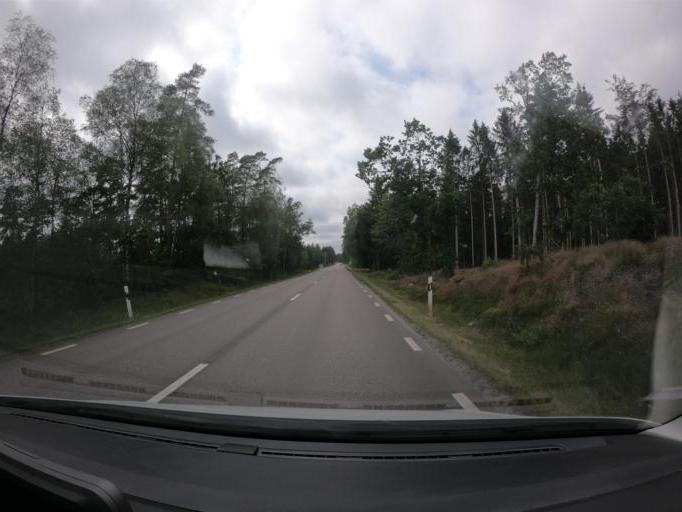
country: SE
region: Skane
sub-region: Perstorps Kommun
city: Perstorp
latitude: 56.2484
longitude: 13.4617
